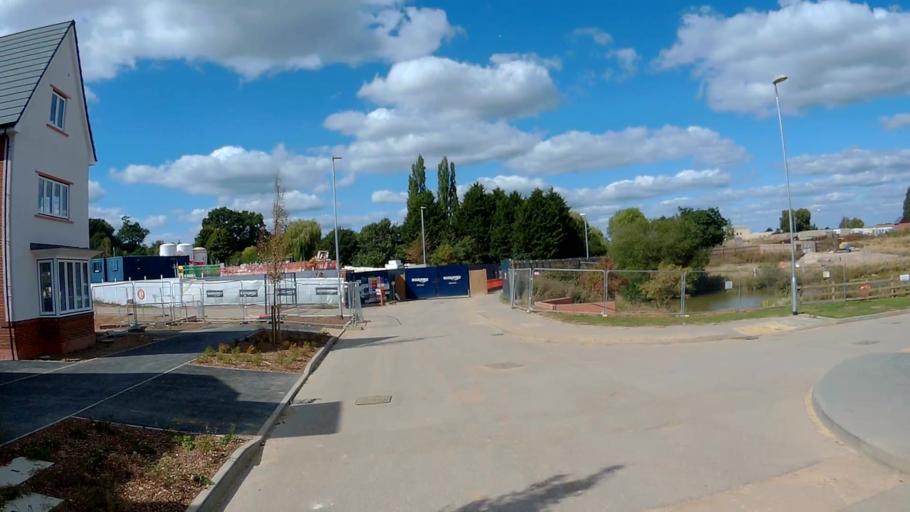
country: GB
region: England
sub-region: Bracknell Forest
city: Binfield
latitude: 51.4251
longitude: -0.7774
